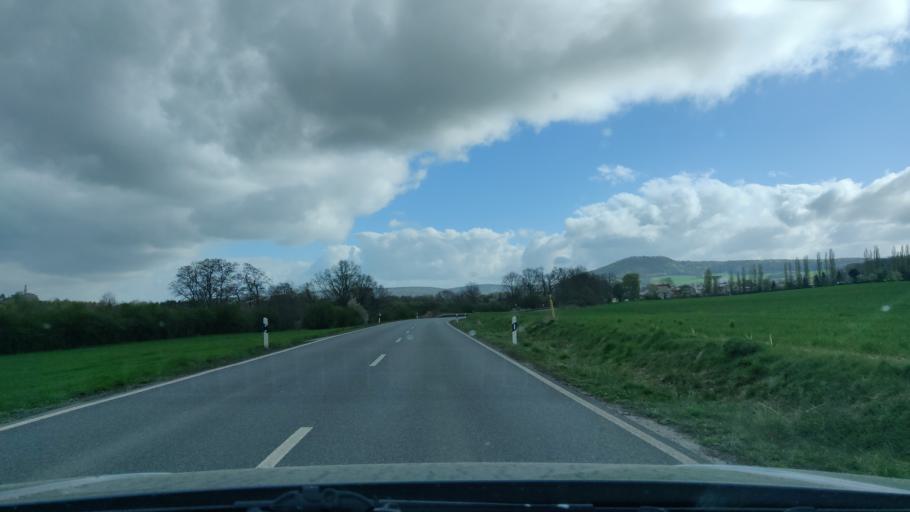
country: DE
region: Hesse
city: Felsberg
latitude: 51.1173
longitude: 9.4122
